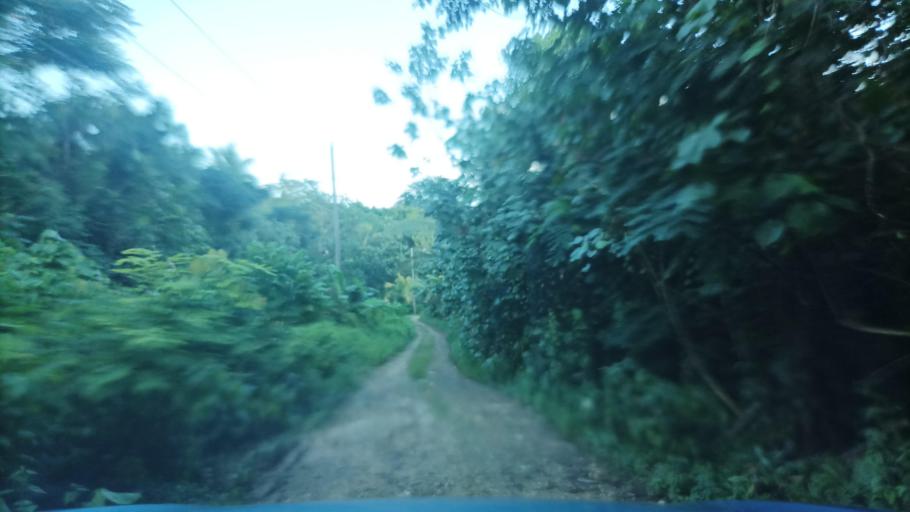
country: FM
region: Pohnpei
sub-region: Kolonia Municipality
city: Kolonia Town
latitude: 6.9755
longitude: 158.1799
